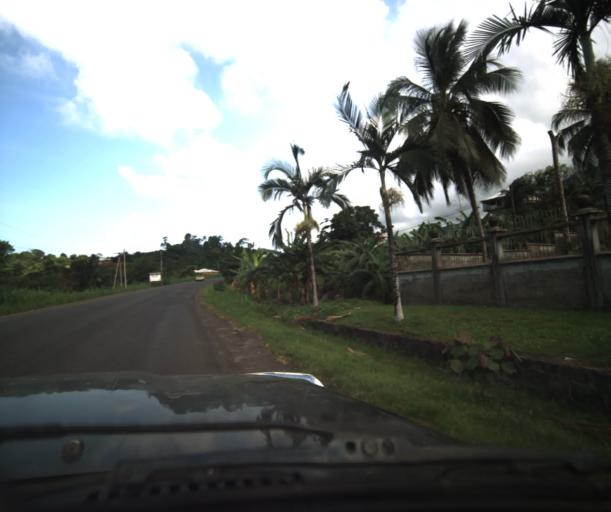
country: CM
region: South-West Province
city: Limbe
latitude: 4.0166
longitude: 9.1414
